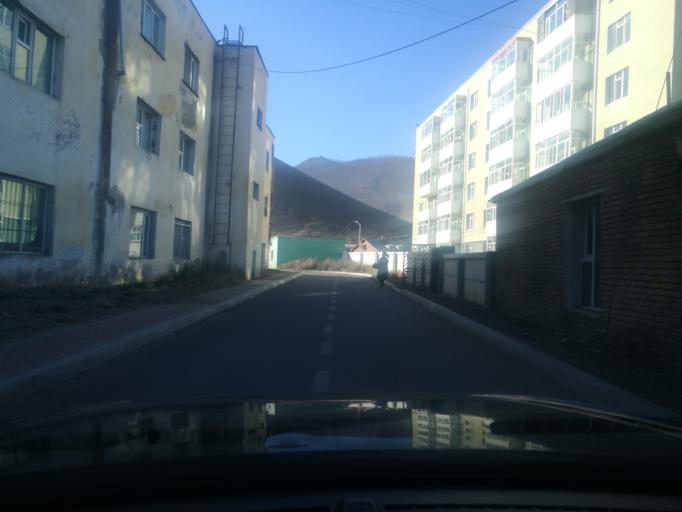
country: MN
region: Ulaanbaatar
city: Ulaanbaatar
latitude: 47.8875
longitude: 106.9043
